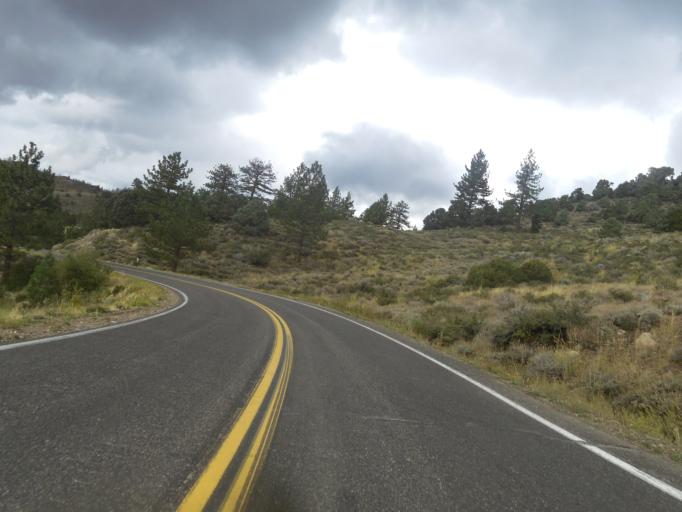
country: US
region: Nevada
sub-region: Douglas County
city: Gardnerville Ranchos
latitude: 38.6715
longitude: -119.6615
